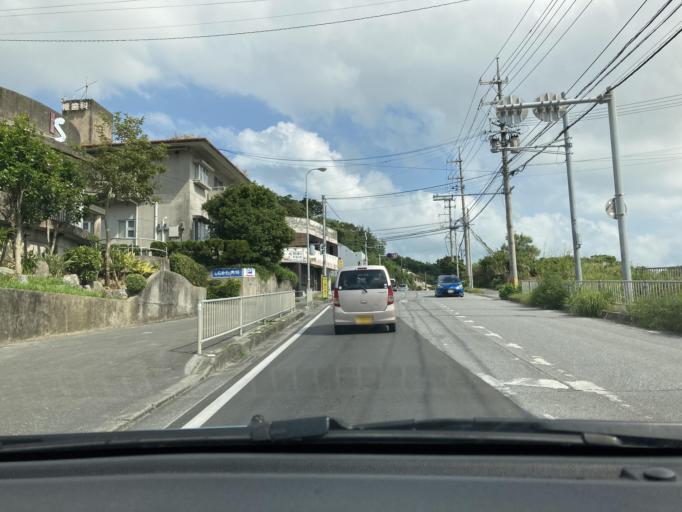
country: JP
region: Okinawa
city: Ginowan
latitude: 26.2417
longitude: 127.7545
